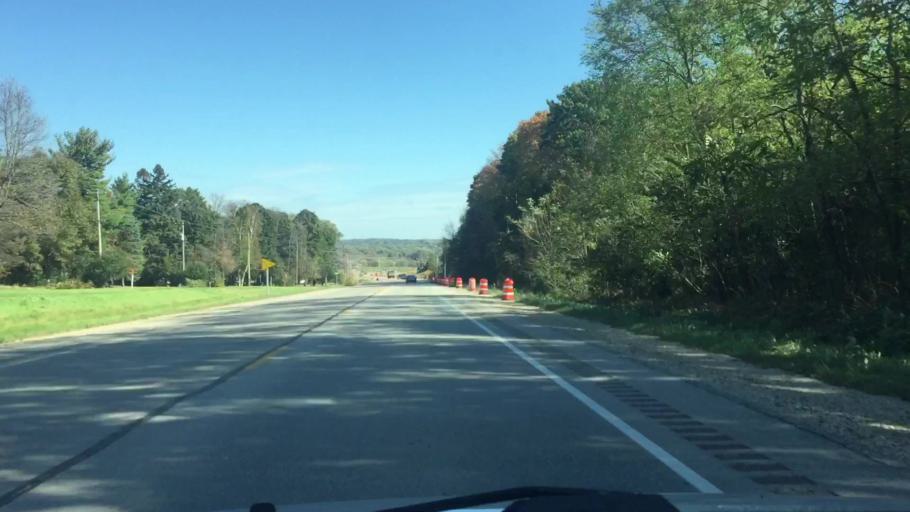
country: US
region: Wisconsin
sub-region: Waukesha County
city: Waukesha
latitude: 42.9776
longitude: -88.2827
